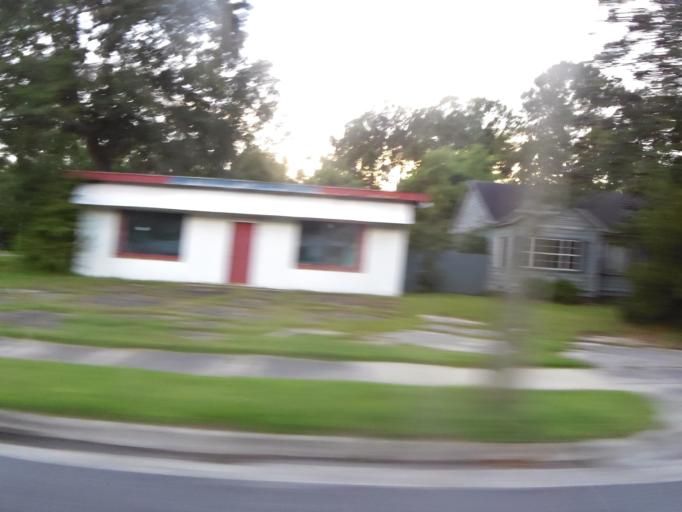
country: US
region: Georgia
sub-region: Camden County
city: Woodbine
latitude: 30.9617
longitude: -81.7225
